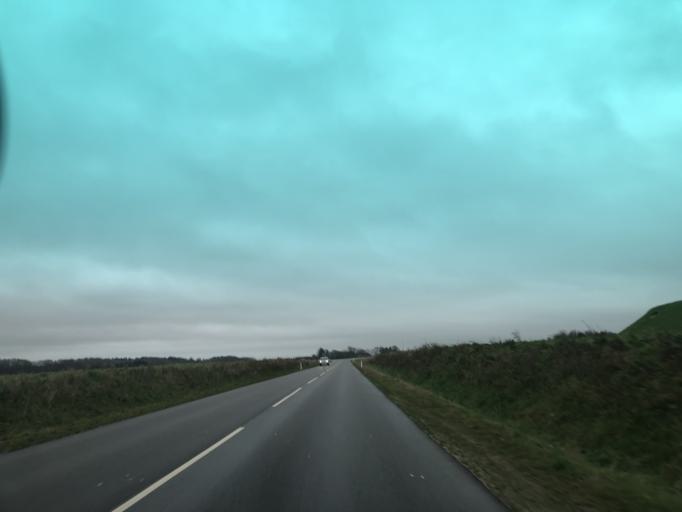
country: DK
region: Central Jutland
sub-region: Randers Kommune
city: Randers
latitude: 56.4167
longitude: 10.0755
